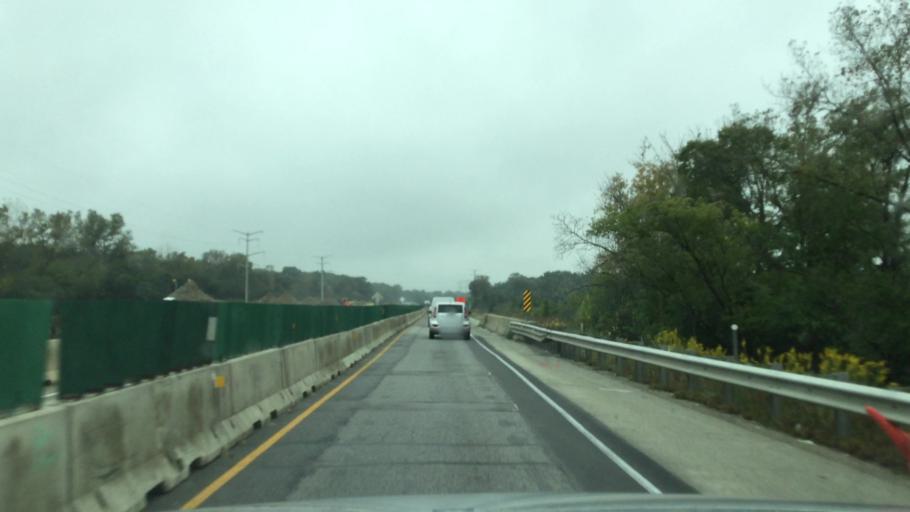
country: US
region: Illinois
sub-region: Cook County
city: Northbrook
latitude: 42.1457
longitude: -87.8136
